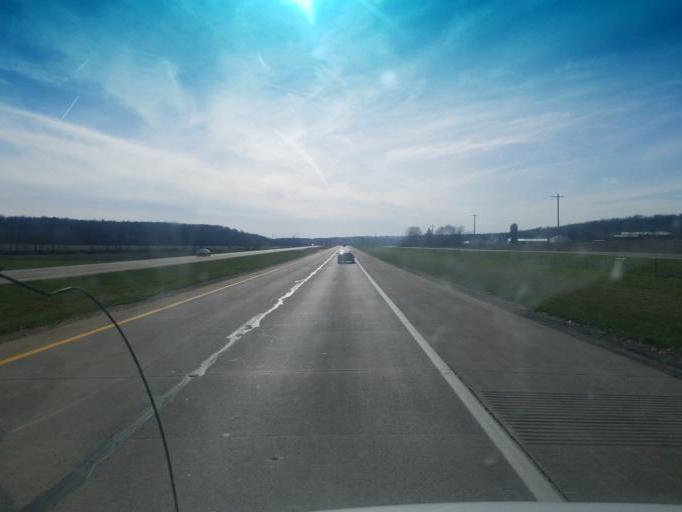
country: US
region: Ohio
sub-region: Logan County
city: Bellefontaine
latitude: 40.3254
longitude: -83.6461
